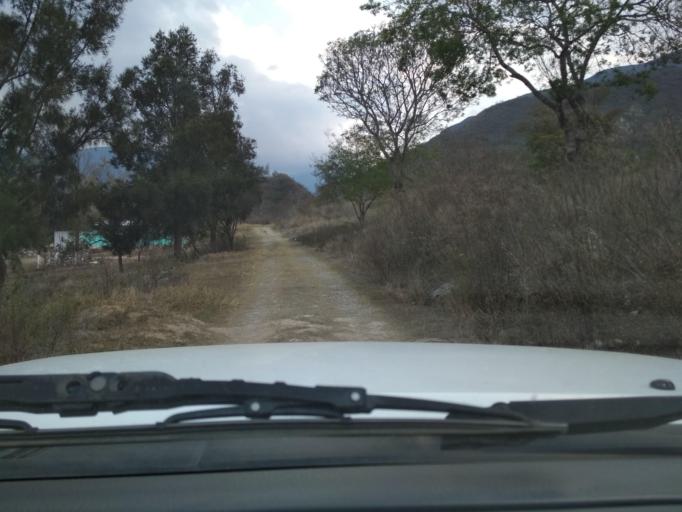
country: MX
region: Veracruz
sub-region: Acultzingo
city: Sierra de Agua
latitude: 18.7727
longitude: -97.2306
